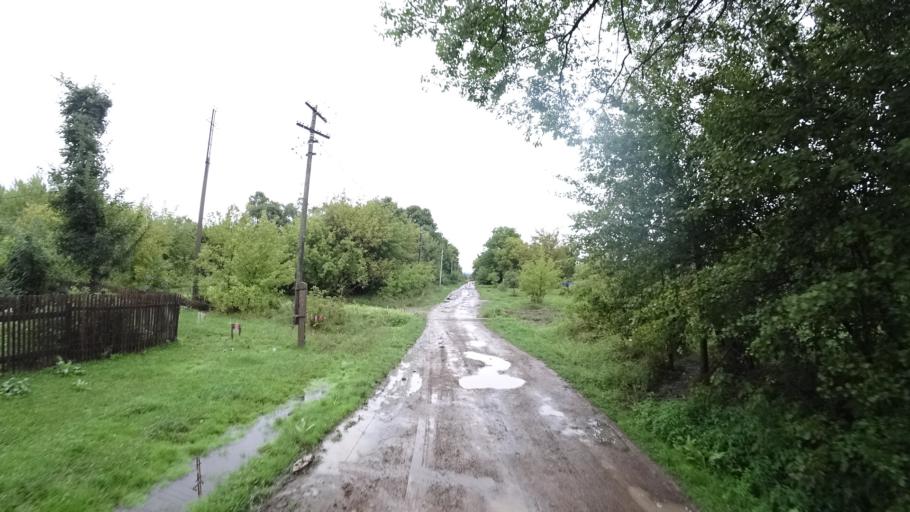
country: RU
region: Primorskiy
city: Monastyrishche
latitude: 44.2528
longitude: 132.4238
